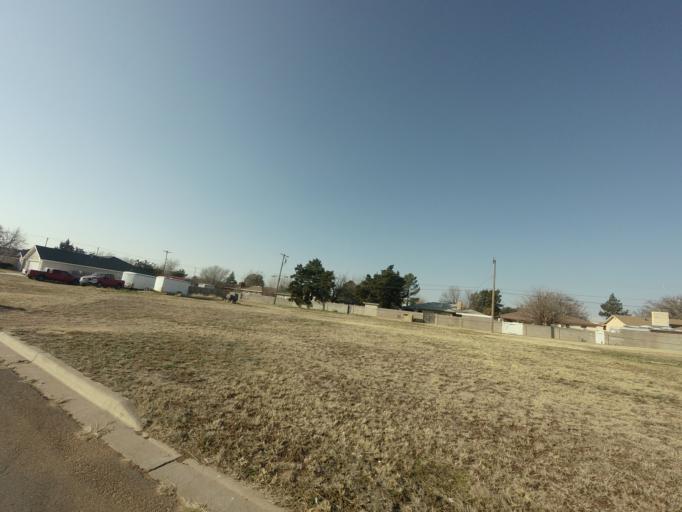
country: US
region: New Mexico
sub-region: Curry County
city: Clovis
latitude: 34.4130
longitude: -103.2115
